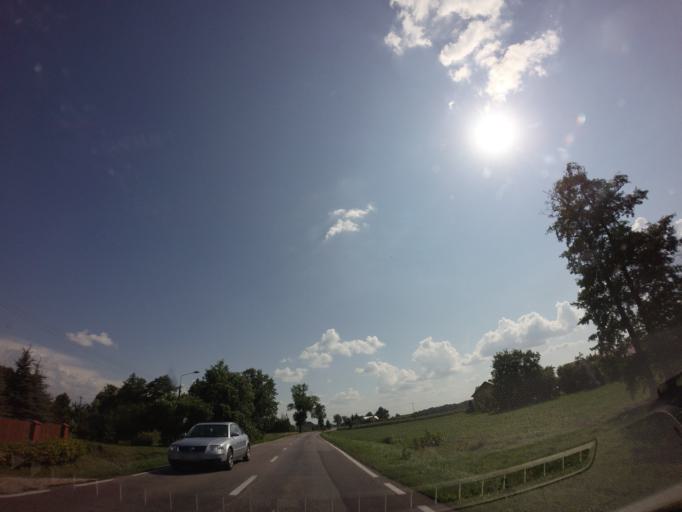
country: PL
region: Podlasie
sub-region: Powiat zambrowski
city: Zambrow
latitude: 52.9004
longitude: 22.2531
